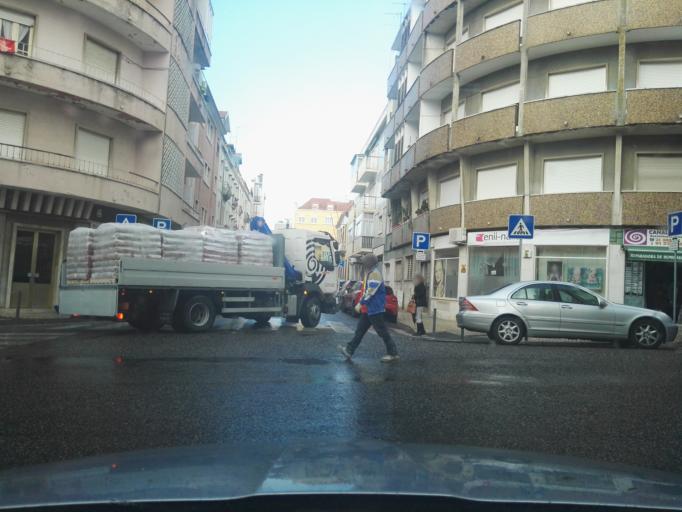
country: PT
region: Lisbon
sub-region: Lisbon
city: Lisbon
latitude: 38.7173
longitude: -9.1631
